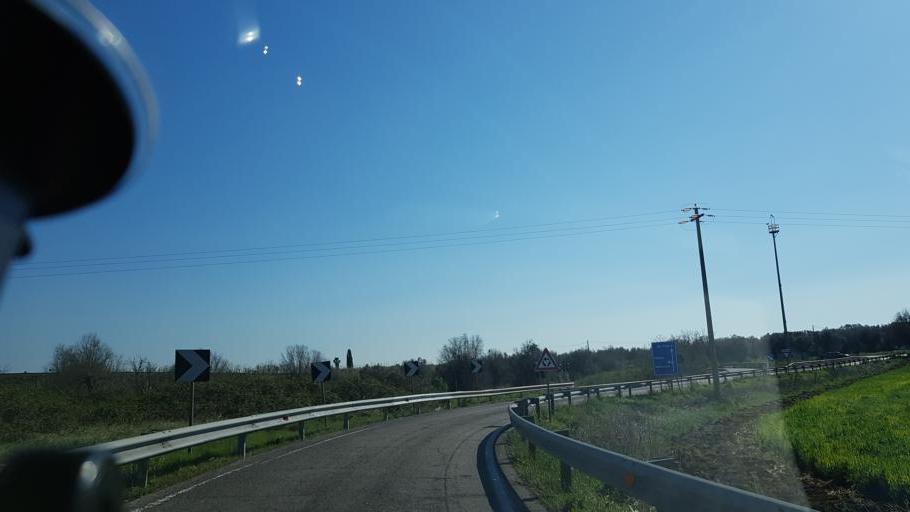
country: IT
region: Apulia
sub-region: Provincia di Brindisi
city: Torchiarolo
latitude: 40.4882
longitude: 18.0394
